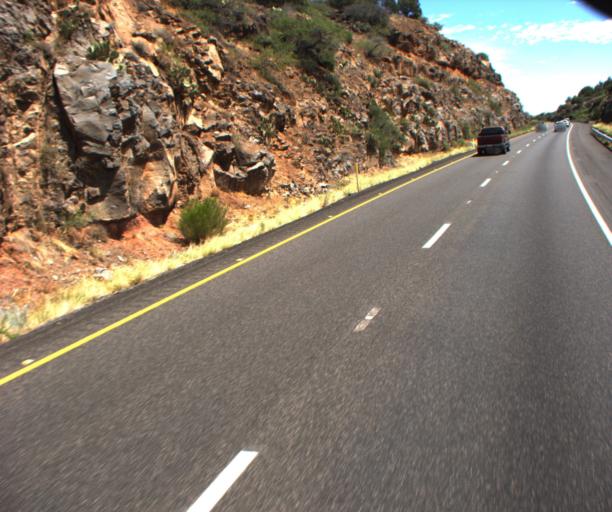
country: US
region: Arizona
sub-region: Yavapai County
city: Big Park
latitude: 34.7163
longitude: -111.7243
